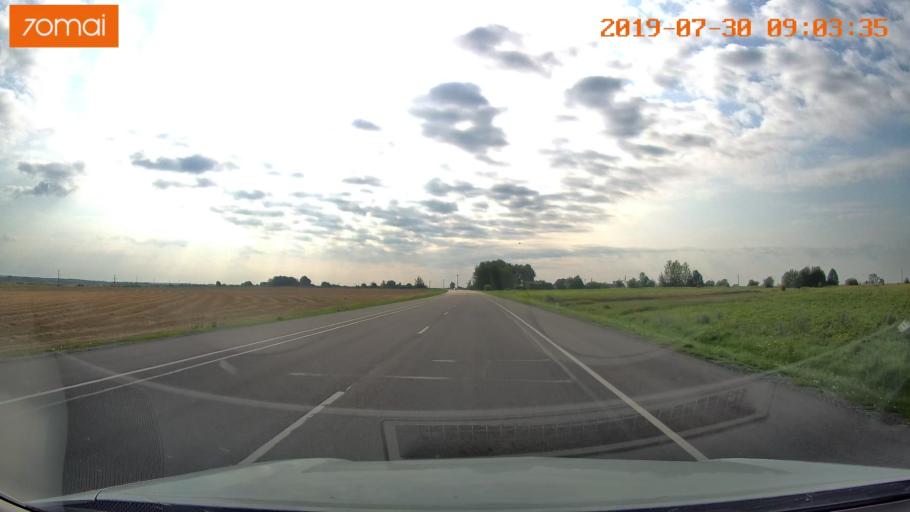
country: RU
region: Kaliningrad
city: Gusev
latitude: 54.6069
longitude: 22.2573
